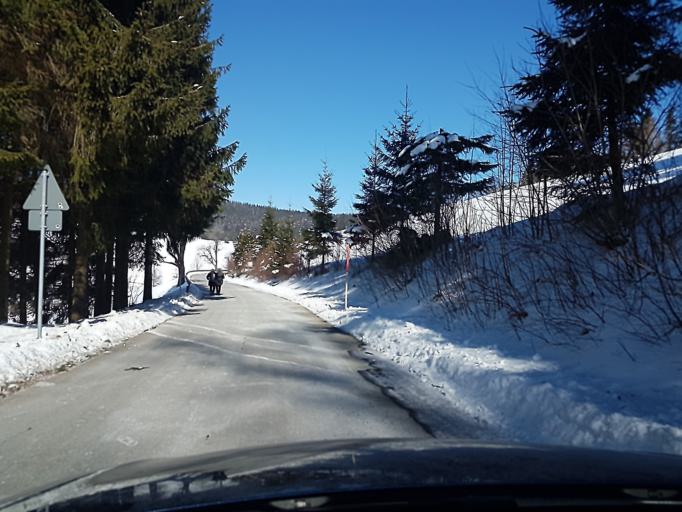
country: DE
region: Baden-Wuerttemberg
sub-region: Freiburg Region
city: Sankt Georgen im Schwarzwald
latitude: 48.1558
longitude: 8.2959
